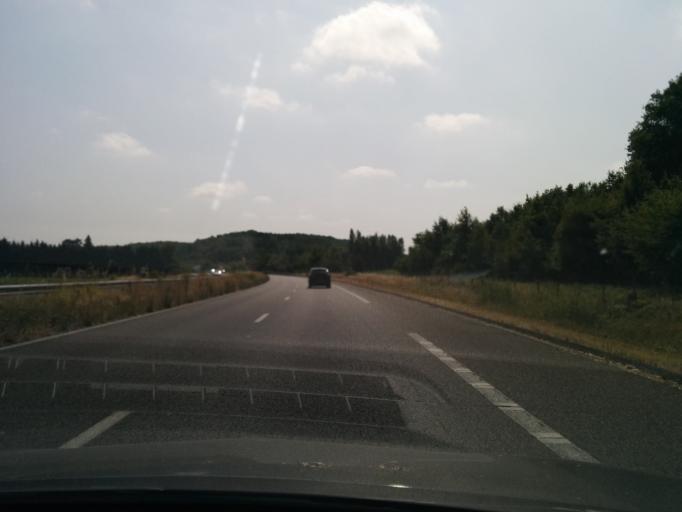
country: FR
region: Midi-Pyrenees
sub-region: Departement de la Haute-Garonne
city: Buzet-sur-Tarn
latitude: 43.7469
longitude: 1.6274
